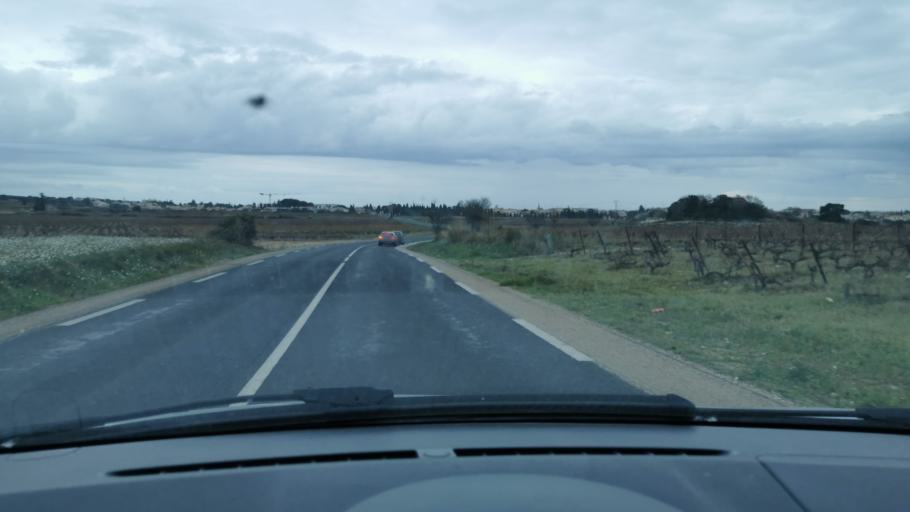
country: FR
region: Languedoc-Roussillon
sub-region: Departement de l'Herault
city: Frontignan
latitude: 43.4480
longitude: 3.7326
